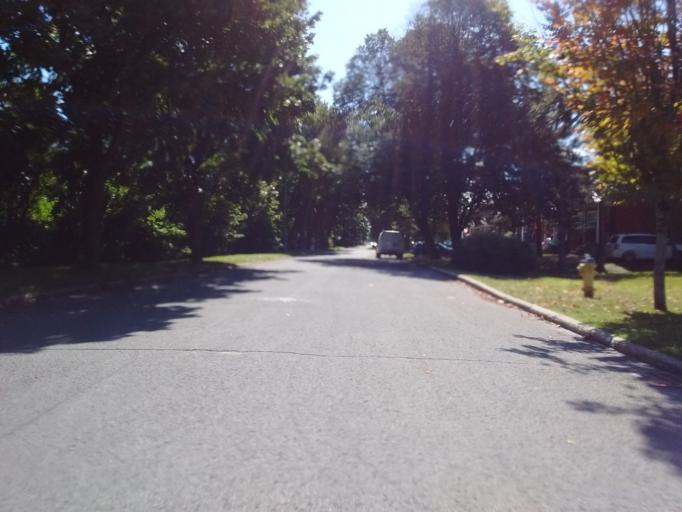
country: CA
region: Ontario
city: Ottawa
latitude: 45.4394
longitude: -75.6376
